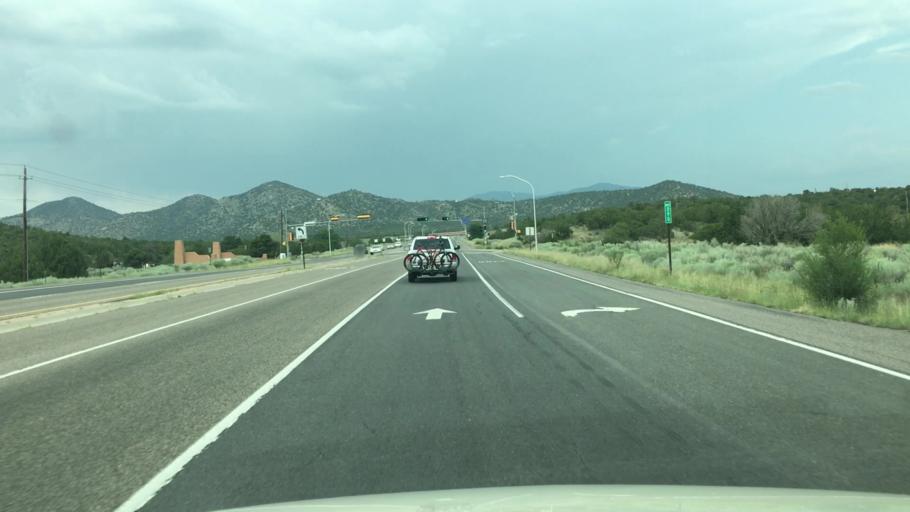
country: US
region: New Mexico
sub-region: Santa Fe County
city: Eldorado at Santa Fe
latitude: 35.5472
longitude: -105.8829
